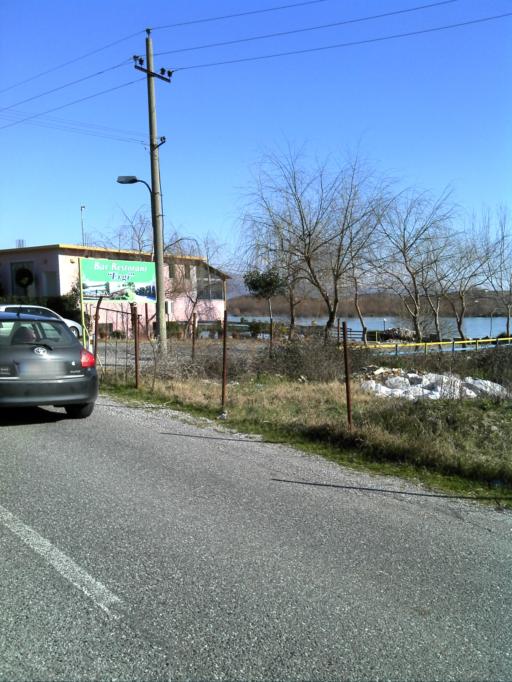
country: AL
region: Shkoder
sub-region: Rrethi i Shkodres
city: Berdica e Madhe
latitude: 42.0308
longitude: 19.4740
